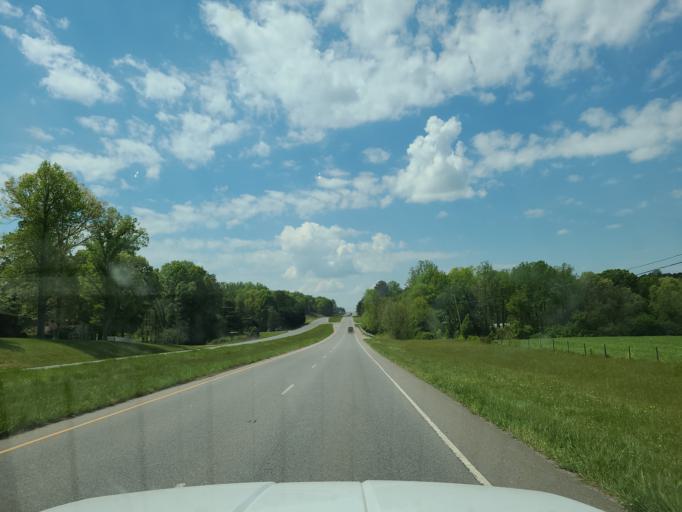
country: US
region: North Carolina
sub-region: Gaston County
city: Cherryville
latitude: 35.4063
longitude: -81.3294
